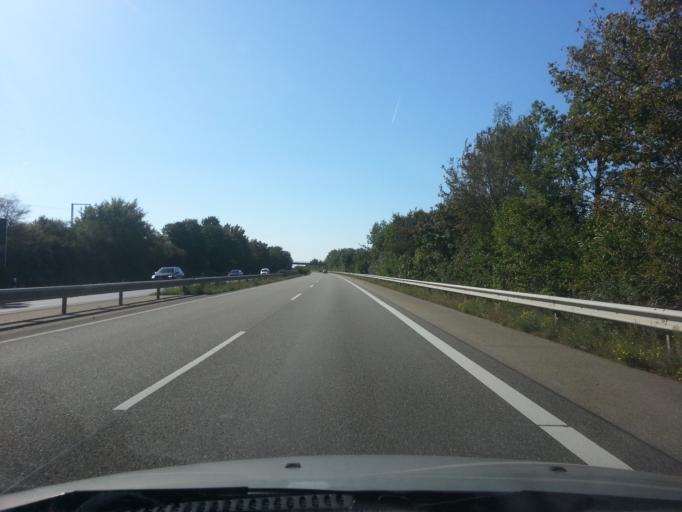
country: DE
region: Baden-Wuerttemberg
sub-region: Karlsruhe Region
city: Hockenheim
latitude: 49.3199
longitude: 8.5374
